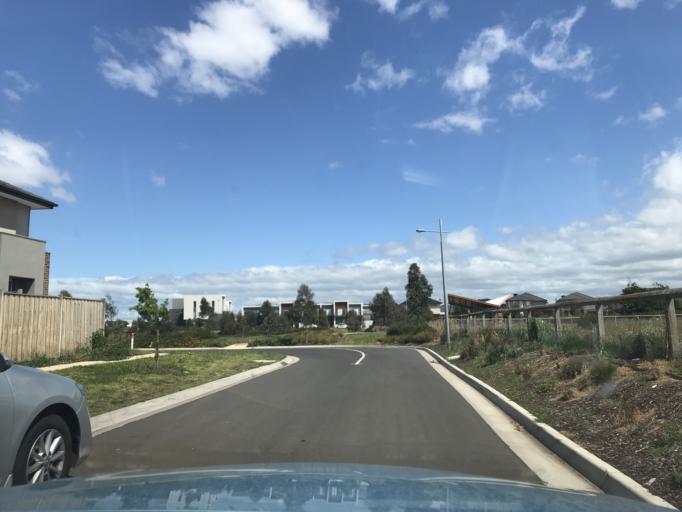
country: AU
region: Victoria
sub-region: Wyndham
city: Williams Landing
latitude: -37.8640
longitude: 144.7400
